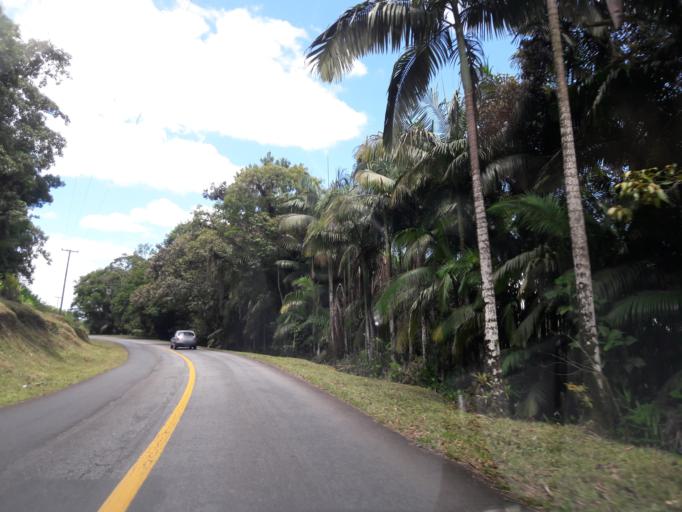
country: BR
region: Parana
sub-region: Antonina
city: Antonina
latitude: -25.4227
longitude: -48.8210
